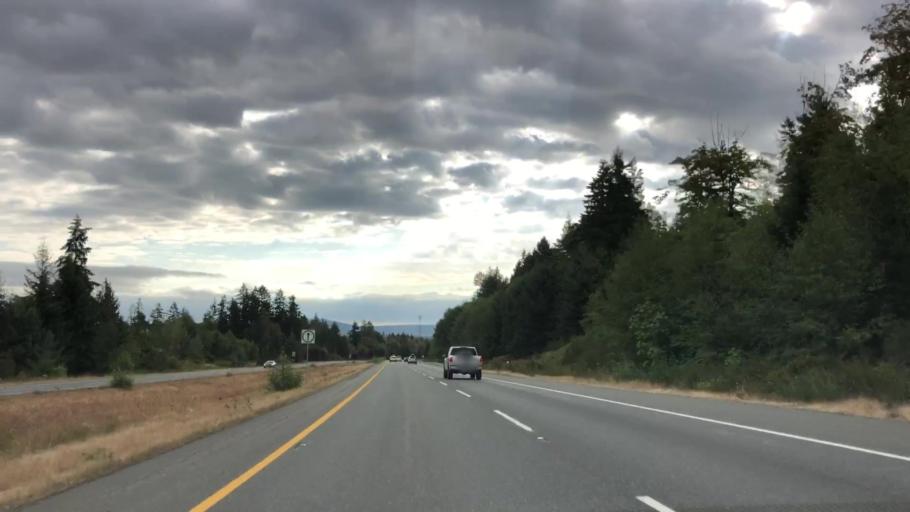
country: CA
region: British Columbia
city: Nanaimo
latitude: 49.1343
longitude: -123.9465
